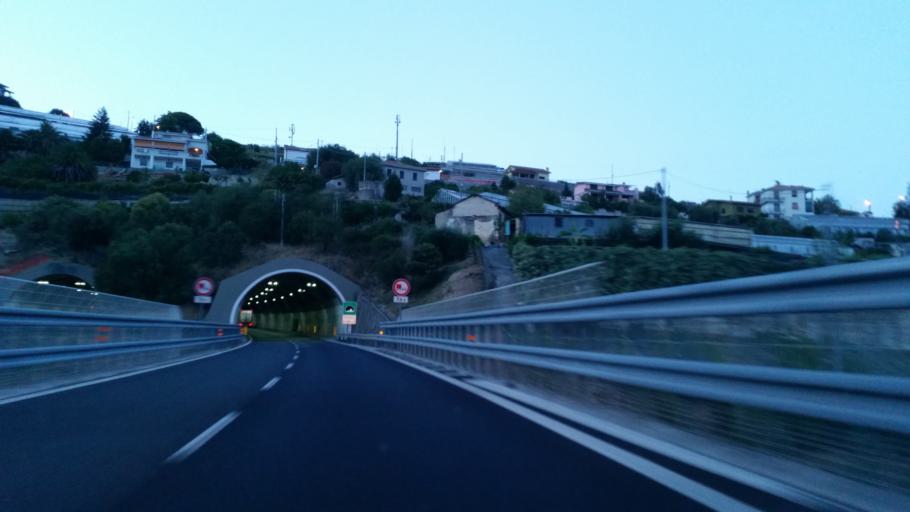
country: IT
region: Liguria
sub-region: Provincia di Imperia
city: San Remo
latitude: 43.8276
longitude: 7.7455
